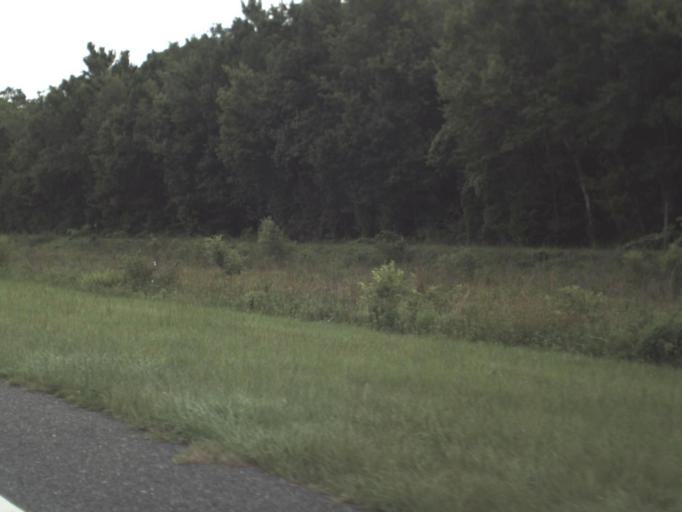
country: US
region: Florida
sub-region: Levy County
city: Williston Highlands
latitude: 29.2385
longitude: -82.7141
